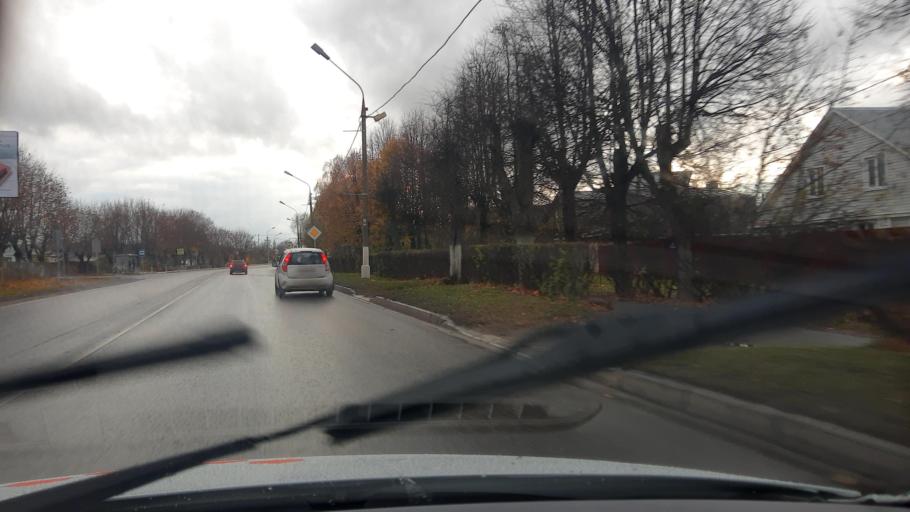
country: RU
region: Moskovskaya
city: Noginsk
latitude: 55.8366
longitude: 38.3890
